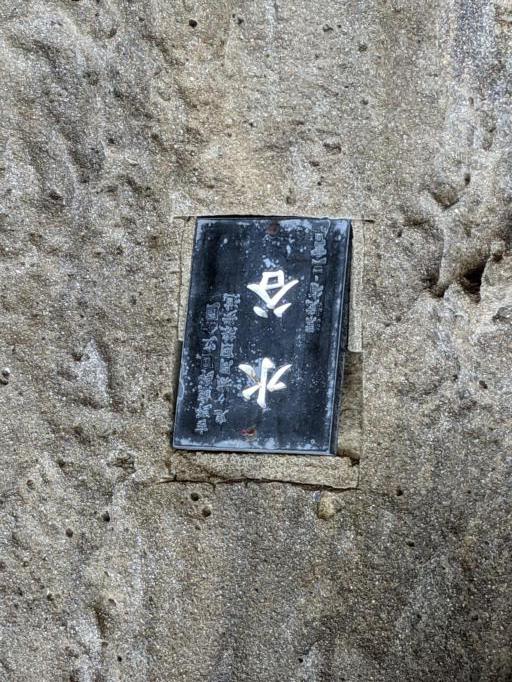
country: JP
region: Mie
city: Owase
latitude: 33.8896
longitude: 136.1115
